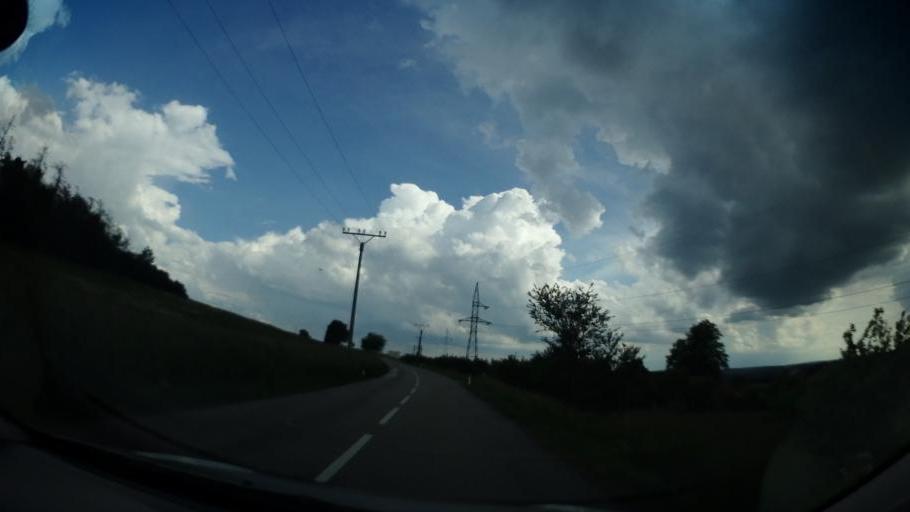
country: CZ
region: South Moravian
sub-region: Okres Brno-Venkov
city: Dolni Loucky
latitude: 49.3962
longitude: 16.3287
